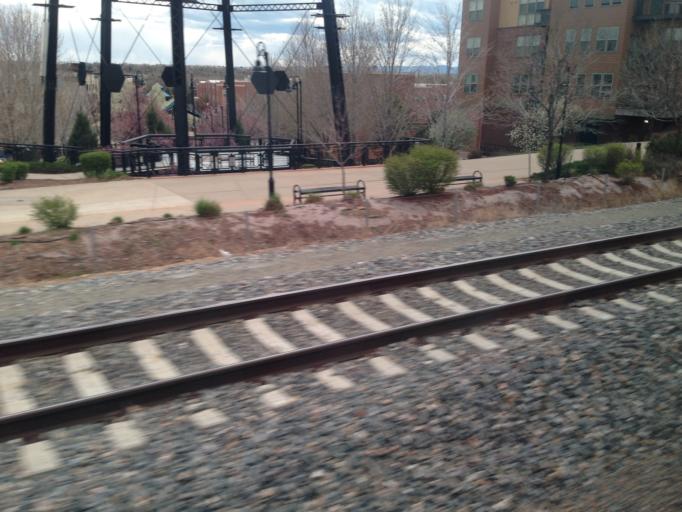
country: US
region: Colorado
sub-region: Jefferson County
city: Arvada
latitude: 39.7980
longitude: -105.0840
